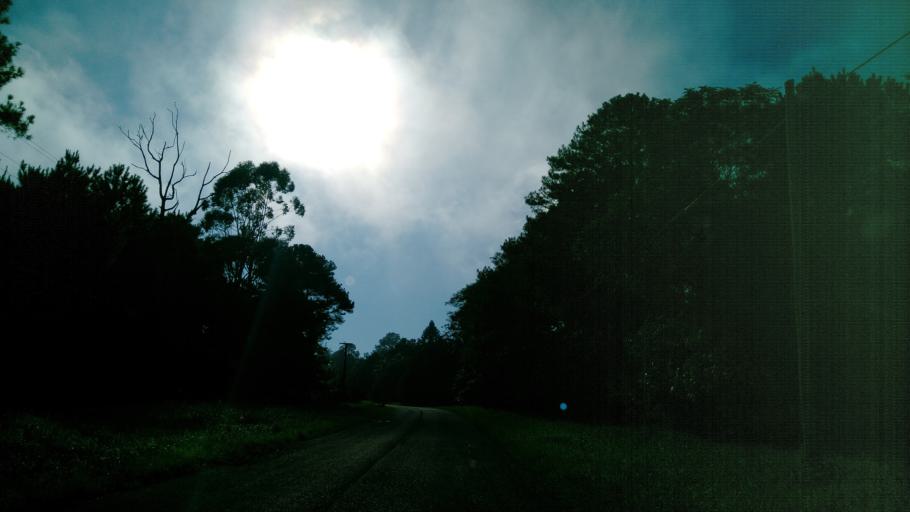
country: AR
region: Misiones
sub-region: Departamento de Montecarlo
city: Montecarlo
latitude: -26.5656
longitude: -54.7894
